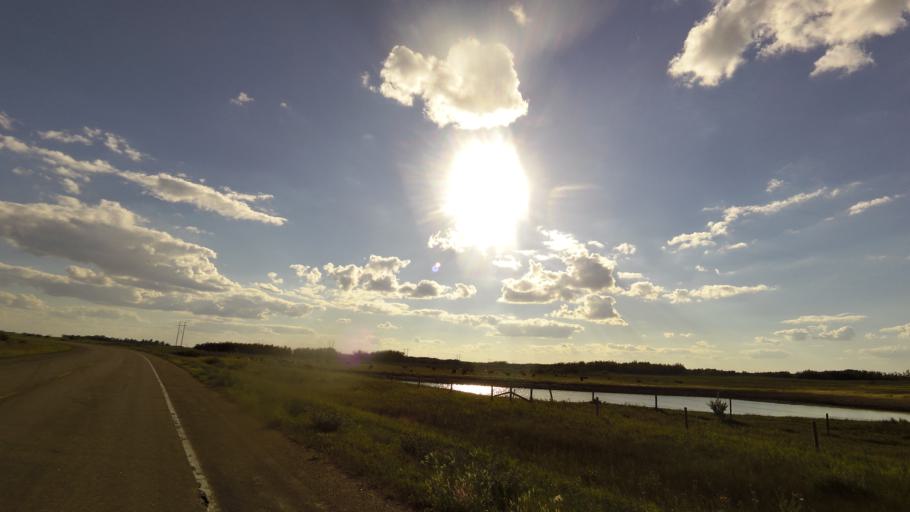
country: CA
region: Saskatchewan
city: Lanigan
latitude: 51.8640
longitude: -105.2124
